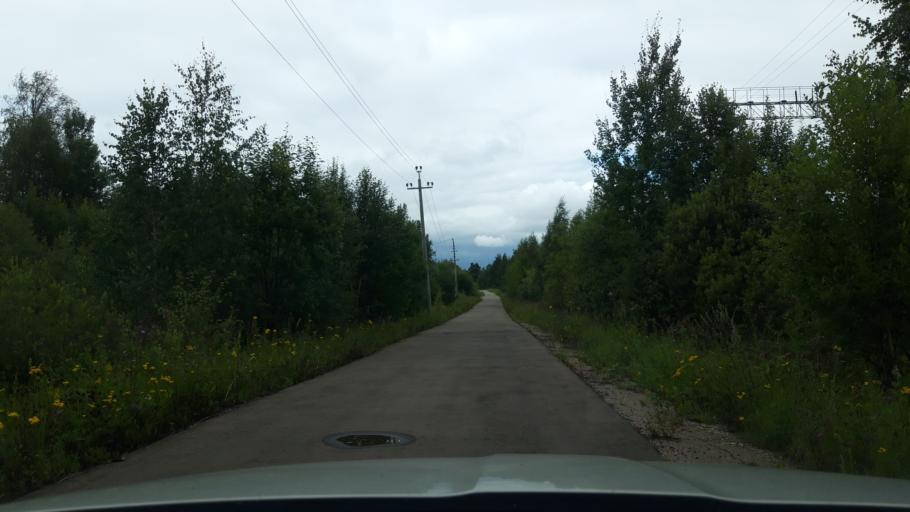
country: RU
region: Moskovskaya
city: Povarovo
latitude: 56.0414
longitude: 37.0543
